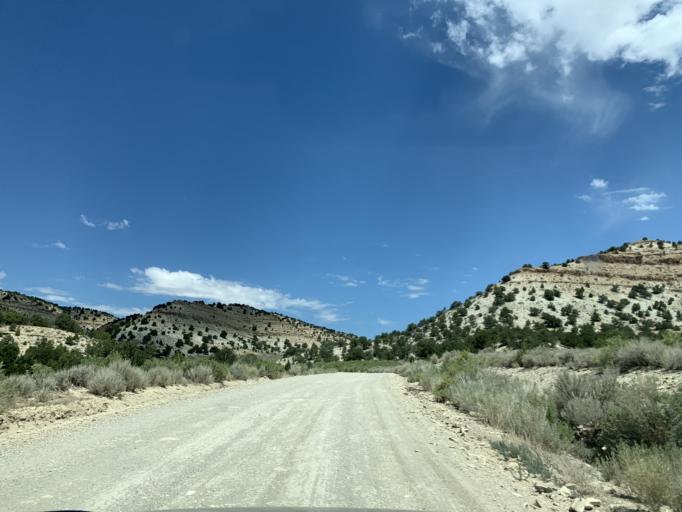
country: US
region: Utah
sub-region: Duchesne County
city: Duchesne
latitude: 39.8648
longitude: -110.2496
